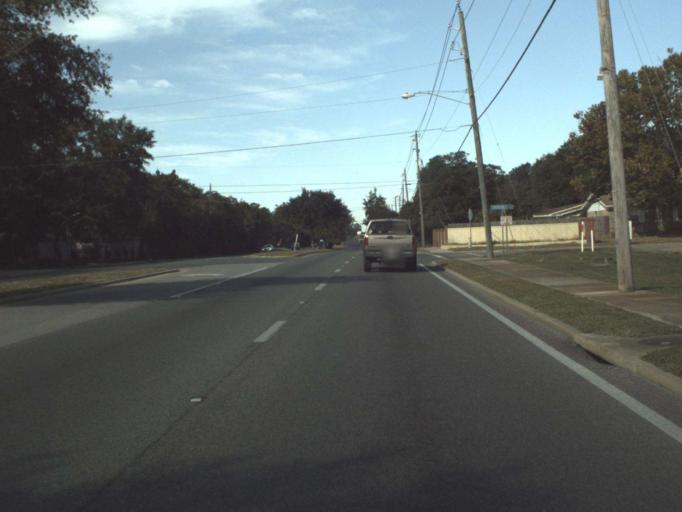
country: US
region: Florida
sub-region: Okaloosa County
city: Mary Esther
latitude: 30.4102
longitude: -86.6774
